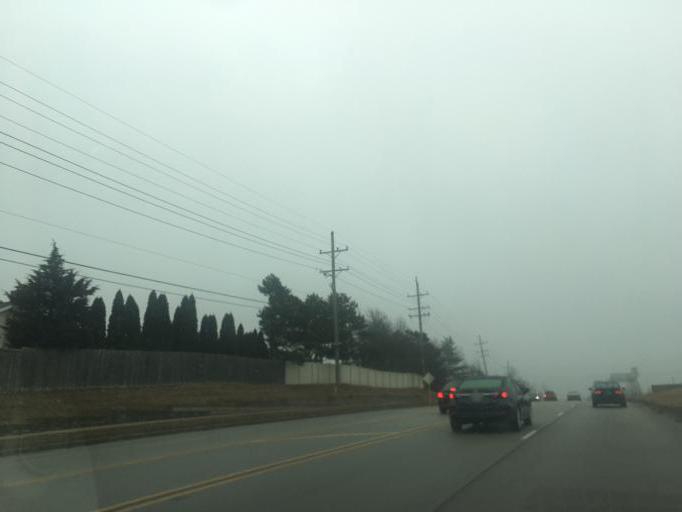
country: US
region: Illinois
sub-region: DuPage County
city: Lisle
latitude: 41.8022
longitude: -88.0645
